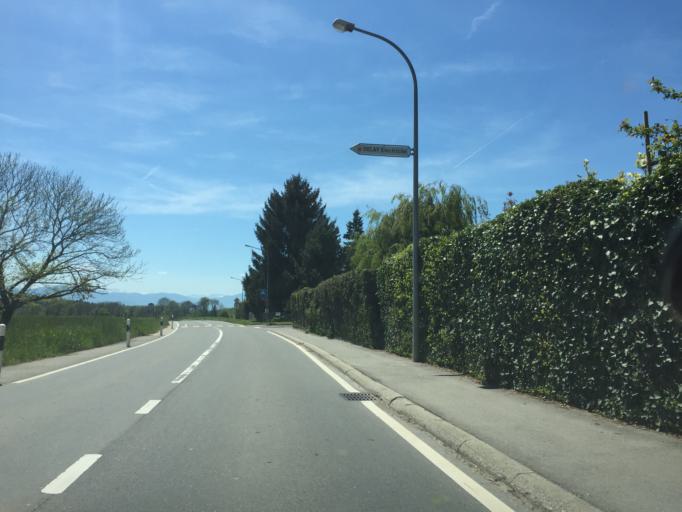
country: CH
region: Vaud
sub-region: Morges District
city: Colombier
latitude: 46.5706
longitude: 6.4545
